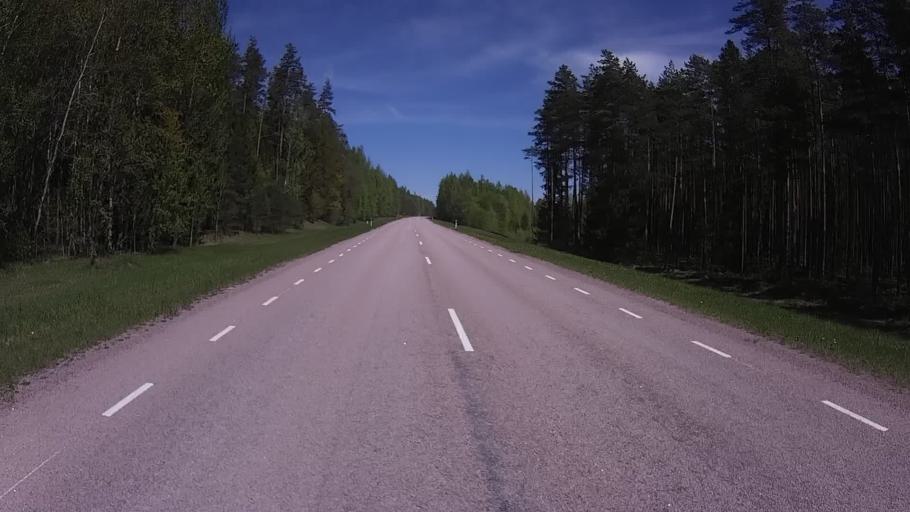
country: EE
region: Vorumaa
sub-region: Voru linn
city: Voru
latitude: 57.7674
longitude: 26.8547
